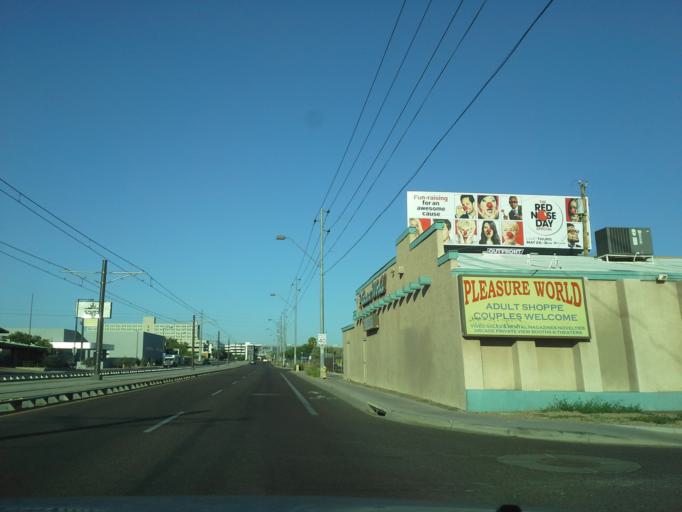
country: US
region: Arizona
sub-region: Maricopa County
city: Tempe Junction
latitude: 33.4480
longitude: -111.9940
